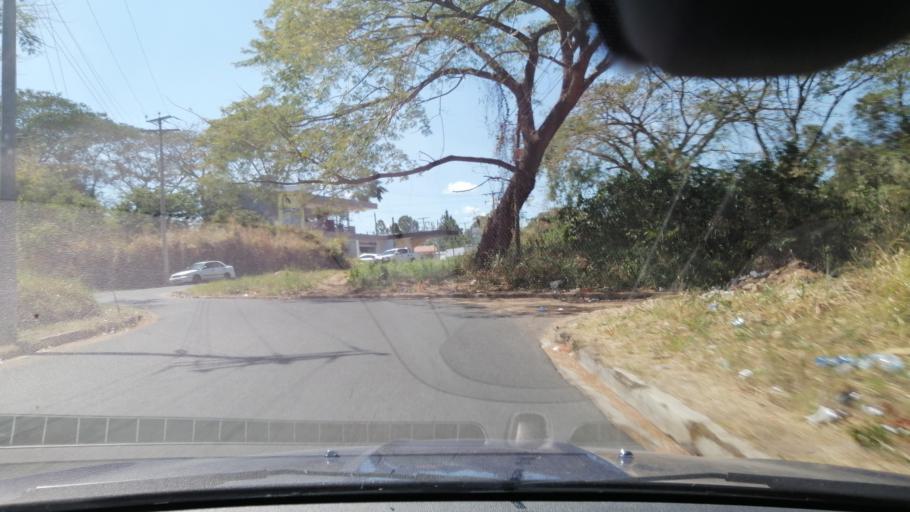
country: SV
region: Santa Ana
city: Santa Ana
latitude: 13.9623
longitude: -89.5747
